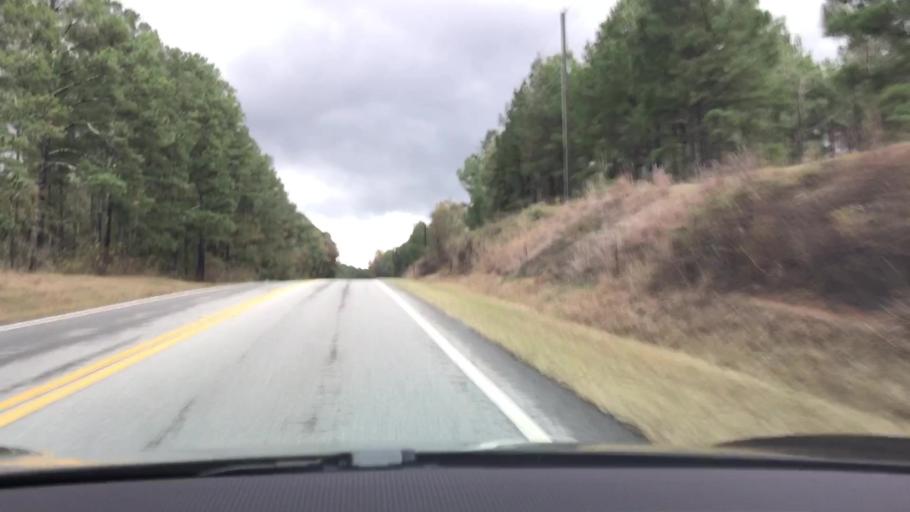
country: US
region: Georgia
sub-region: Greene County
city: Greensboro
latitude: 33.7054
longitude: -83.2878
